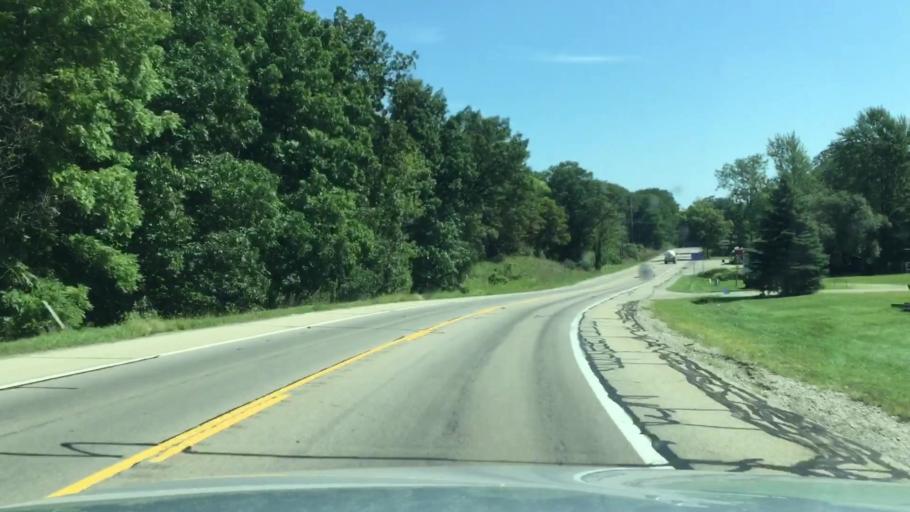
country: US
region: Michigan
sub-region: Jackson County
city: Brooklyn
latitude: 42.0590
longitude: -84.1336
